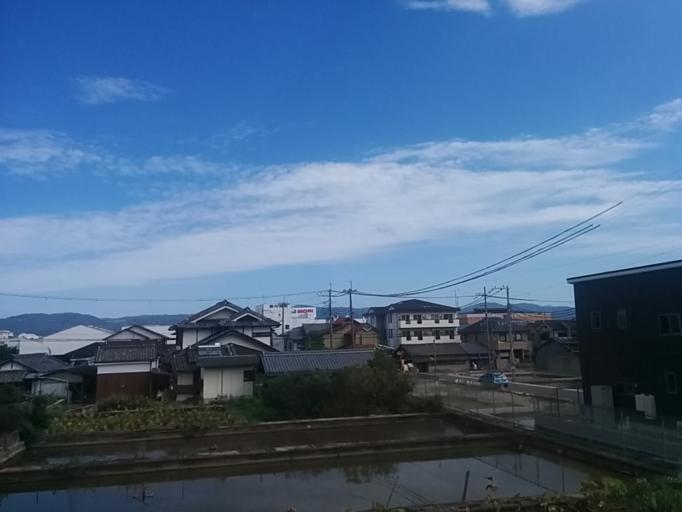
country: JP
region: Nara
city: Nara-shi
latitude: 34.6559
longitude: 135.7824
